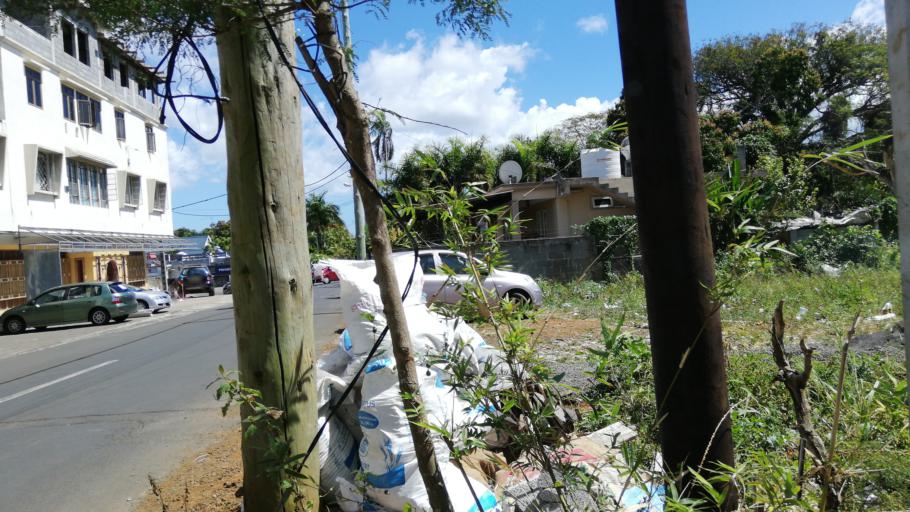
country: MU
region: Moka
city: Moka
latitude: -20.2258
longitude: 57.4711
